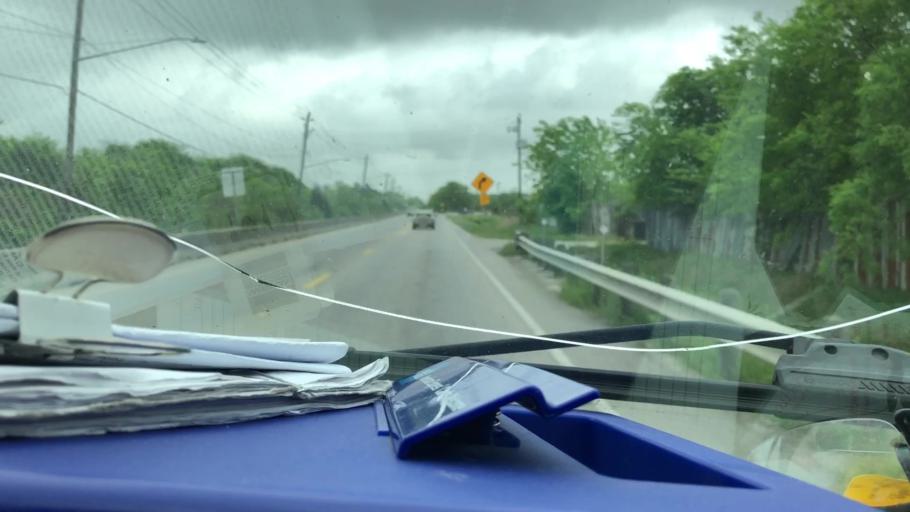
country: US
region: Texas
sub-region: Galveston County
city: Bacliff
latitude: 29.4878
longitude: -94.9679
